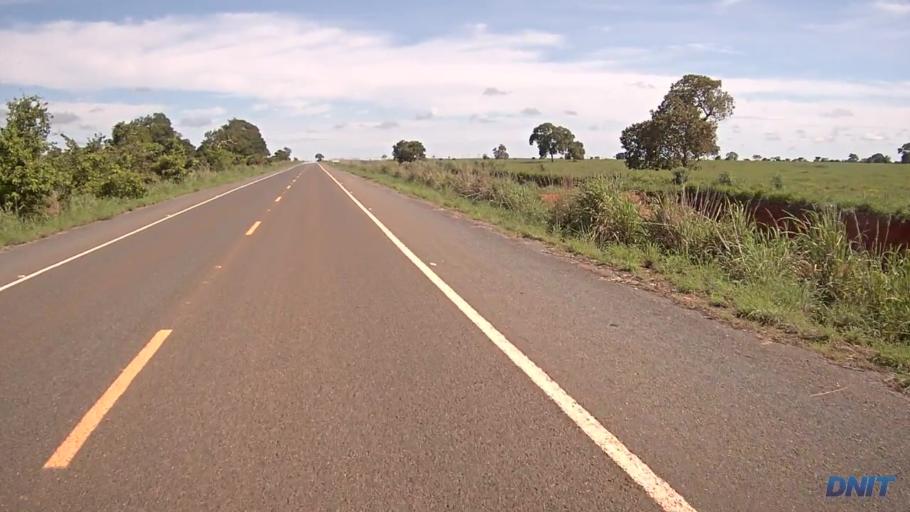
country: BR
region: Goias
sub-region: Sao Miguel Do Araguaia
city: Sao Miguel do Araguaia
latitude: -13.4434
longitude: -50.1227
